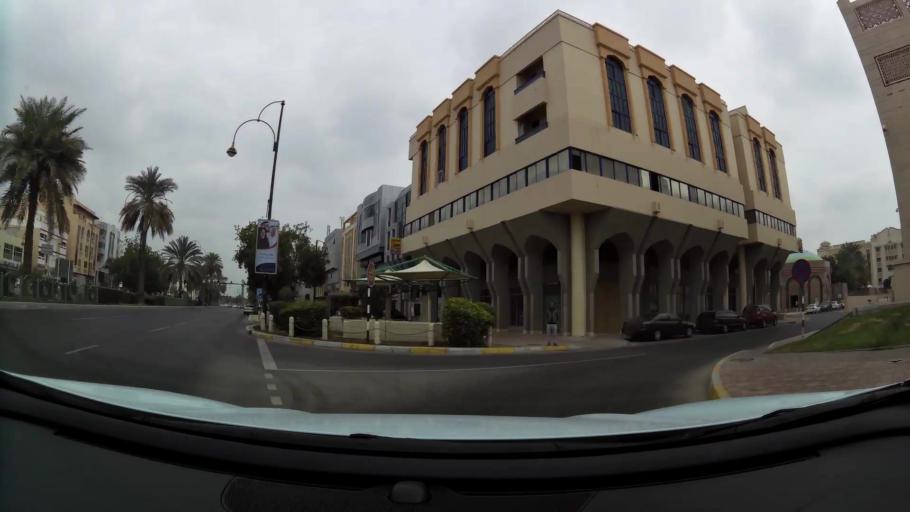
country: AE
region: Abu Dhabi
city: Al Ain
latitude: 24.2231
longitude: 55.7660
